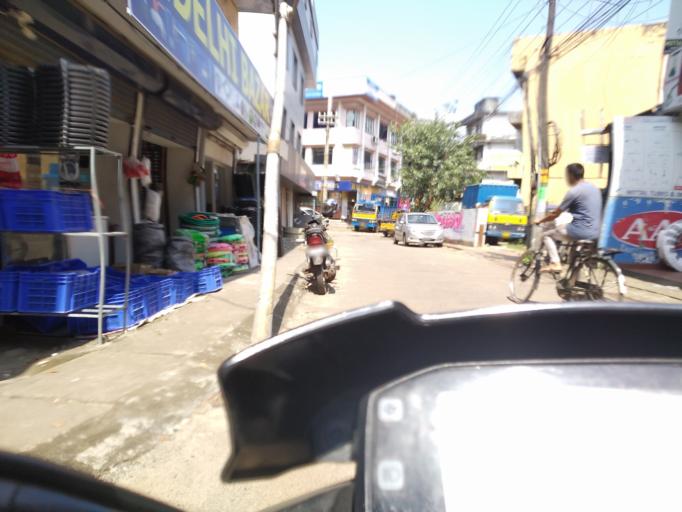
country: IN
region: Kerala
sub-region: Ernakulam
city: Cochin
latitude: 9.9789
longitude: 76.2818
